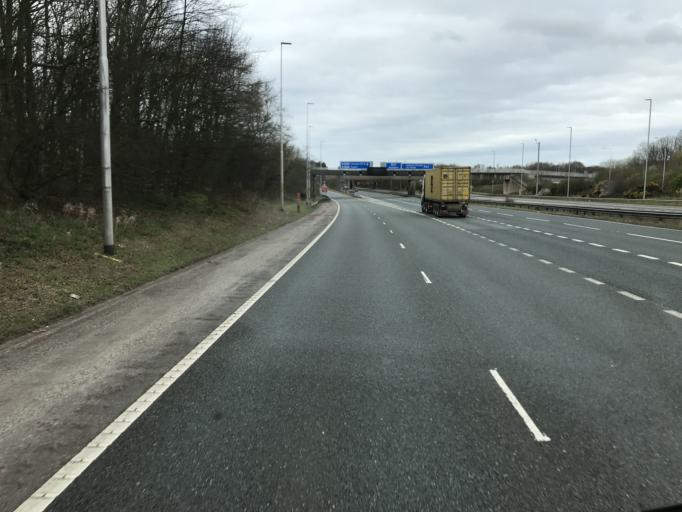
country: GB
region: England
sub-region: Knowsley
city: Whiston
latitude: 53.4003
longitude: -2.8004
